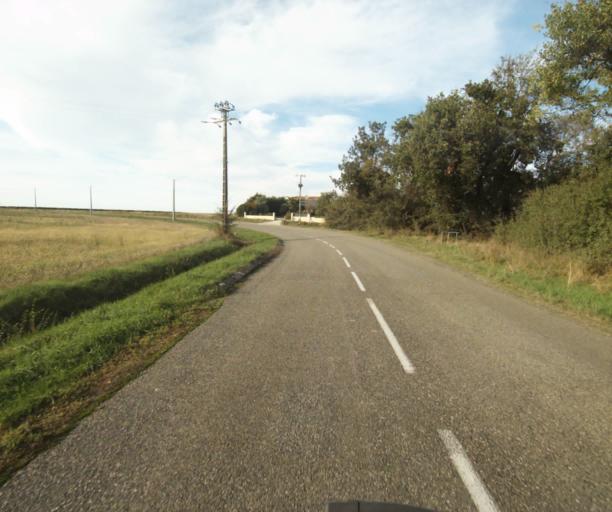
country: FR
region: Midi-Pyrenees
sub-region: Departement du Tarn-et-Garonne
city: Finhan
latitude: 43.9031
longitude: 1.1242
